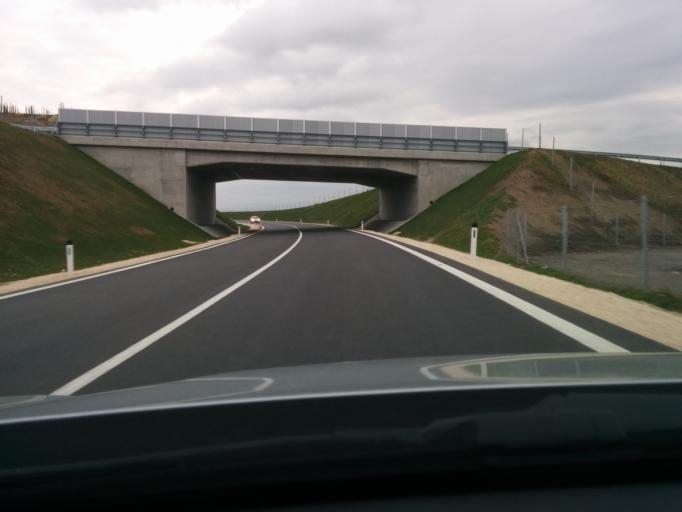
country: AT
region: Lower Austria
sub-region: Politischer Bezirk Mistelbach
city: Mistelbach
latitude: 48.5711
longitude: 16.5541
